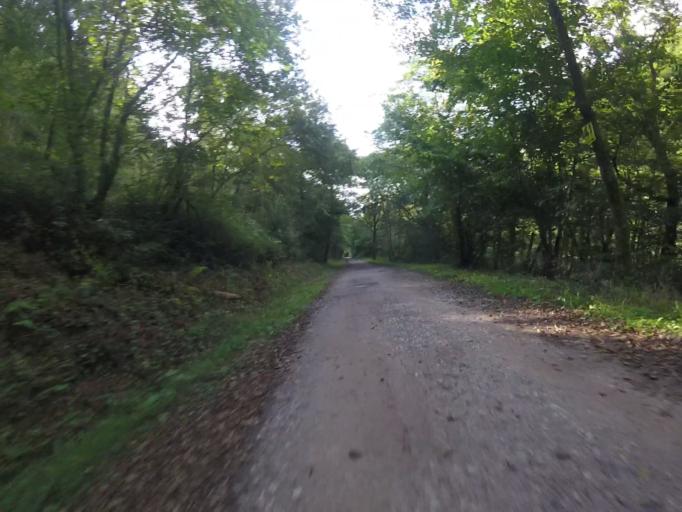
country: ES
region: Basque Country
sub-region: Provincia de Guipuzcoa
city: Elduayen
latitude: 43.1815
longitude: -1.9940
